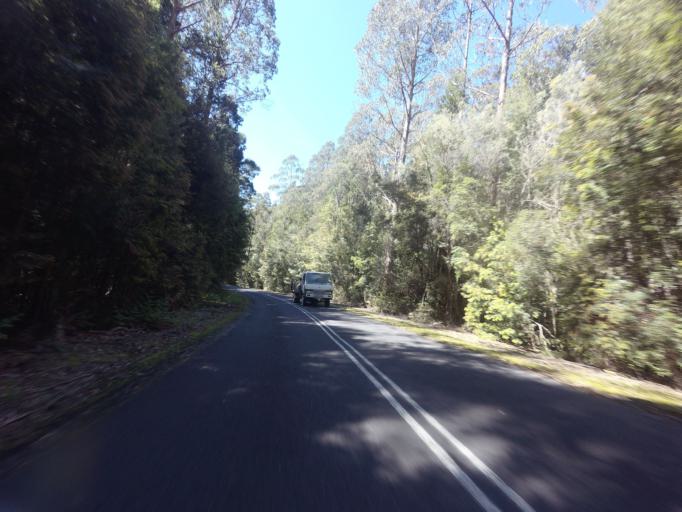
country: AU
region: Tasmania
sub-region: Huon Valley
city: Geeveston
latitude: -42.8233
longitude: 146.3325
